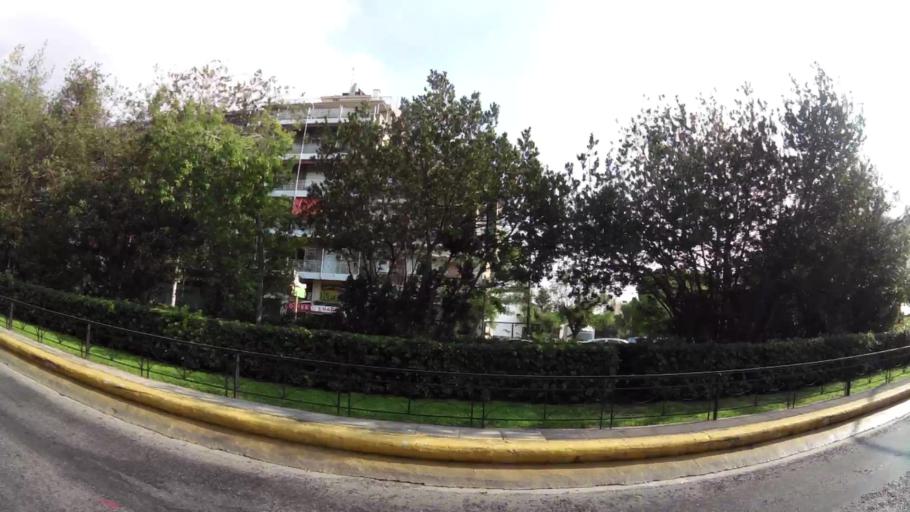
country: GR
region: Attica
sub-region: Nomarchia Athinas
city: Moskhaton
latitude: 37.9473
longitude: 23.6883
